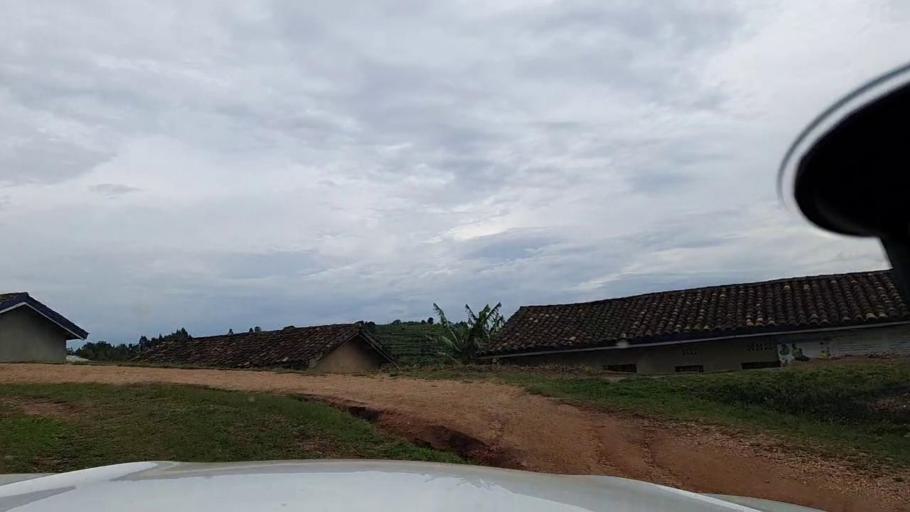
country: RW
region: Southern Province
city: Gitarama
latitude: -2.1273
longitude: 29.6543
